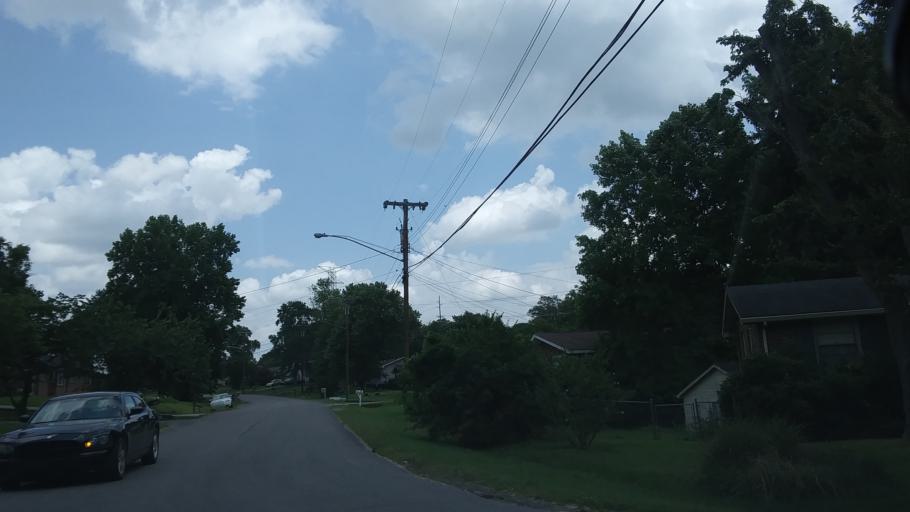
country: US
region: Tennessee
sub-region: Davidson County
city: Belle Meade
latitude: 36.1509
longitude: -86.8866
